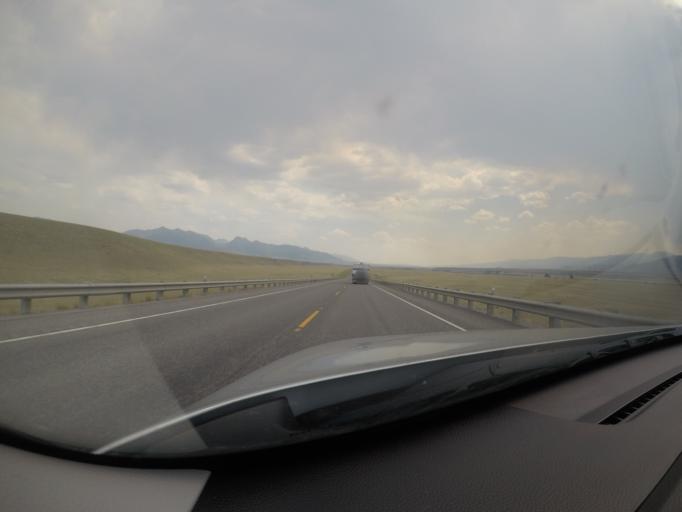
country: US
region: Montana
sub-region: Madison County
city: Virginia City
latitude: 45.1397
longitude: -111.6745
